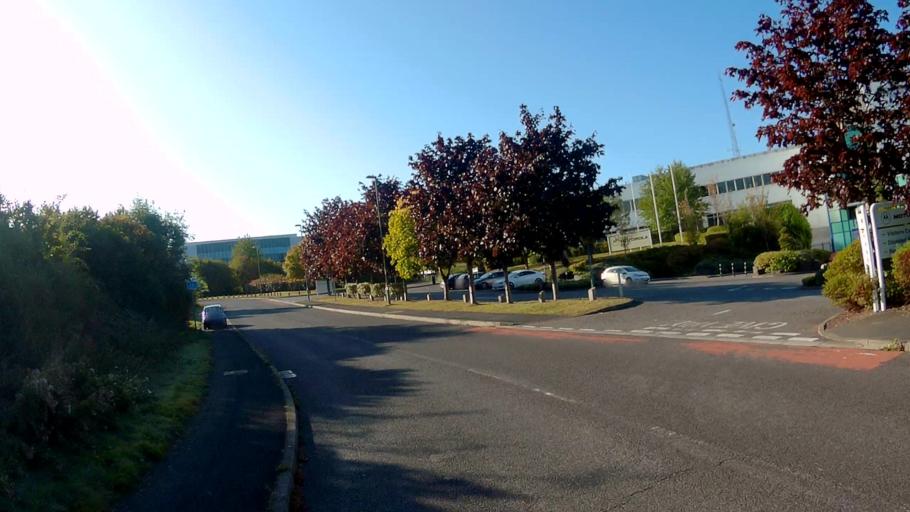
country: GB
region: England
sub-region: Hampshire
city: Basingstoke
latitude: 51.2455
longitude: -1.0992
